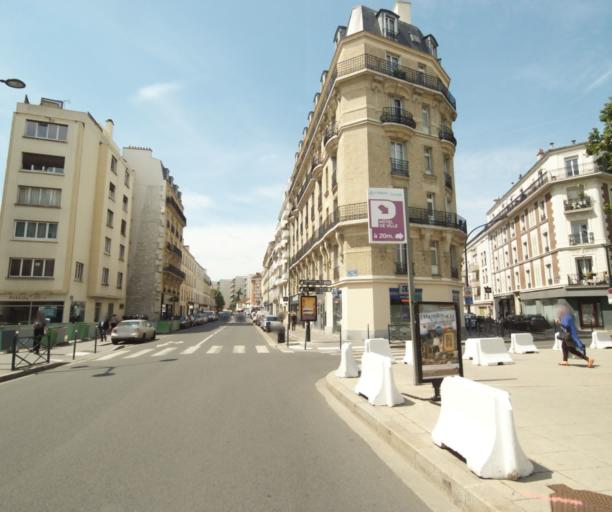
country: FR
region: Ile-de-France
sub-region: Departement des Hauts-de-Seine
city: Asnieres-sur-Seine
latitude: 48.9101
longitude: 2.2882
